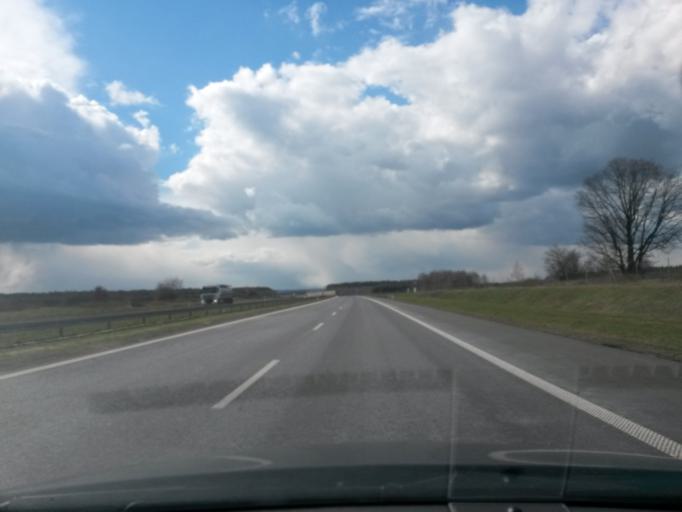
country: PL
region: Greater Poland Voivodeship
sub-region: Powiat turecki
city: Wladyslawow
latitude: 52.1523
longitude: 18.4774
